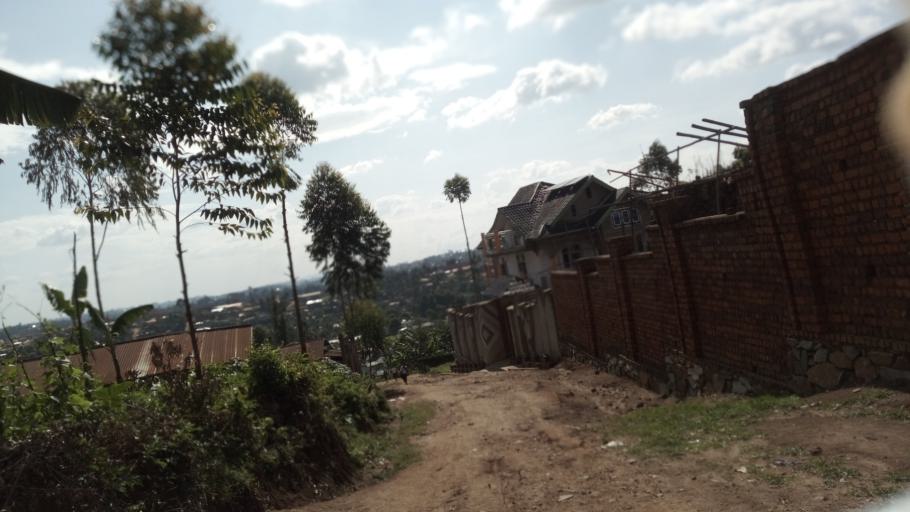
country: CD
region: Nord Kivu
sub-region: North Kivu
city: Butembo
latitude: 0.1098
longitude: 29.3240
